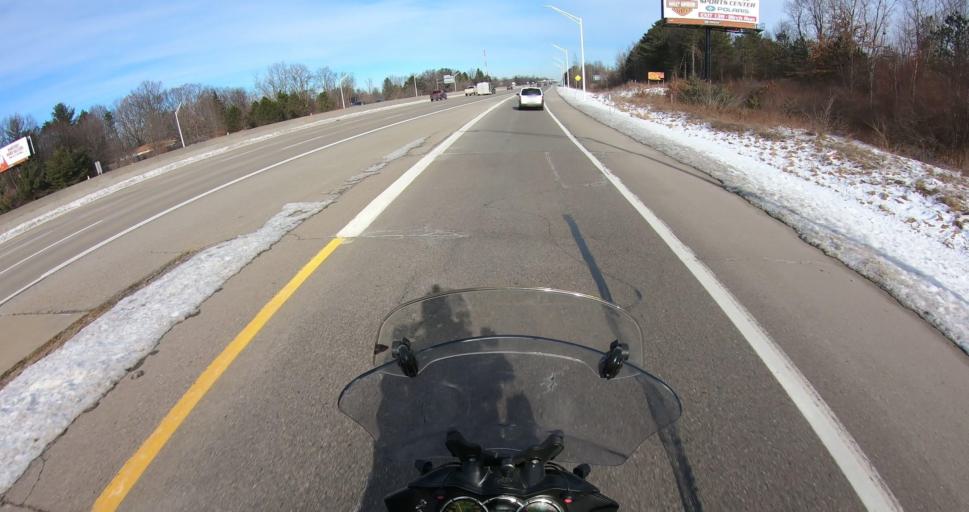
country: US
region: Michigan
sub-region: Genesee County
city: Clio
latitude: 43.1845
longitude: -83.7665
